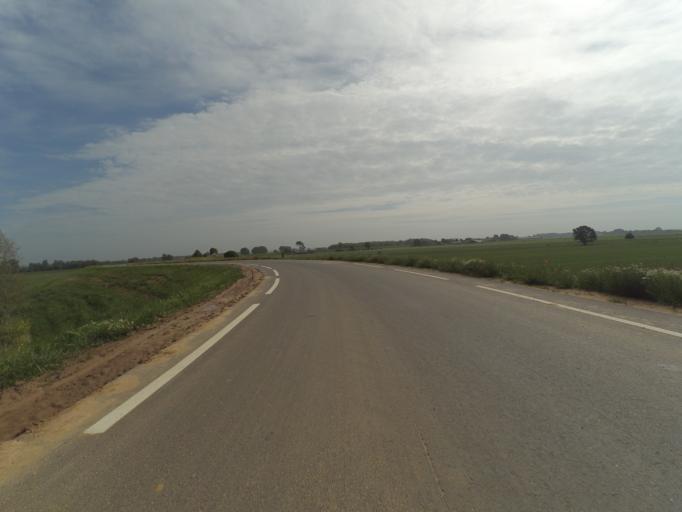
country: NL
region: Utrecht
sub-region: Gemeente Wijk bij Duurstede
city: Wijk bij Duurstede
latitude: 51.9631
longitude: 5.3759
